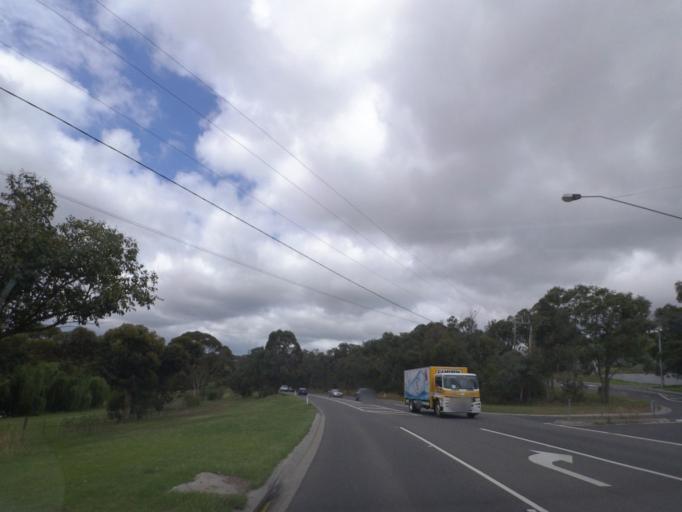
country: AU
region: Victoria
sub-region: Nillumbik
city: Diamond Creek
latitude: -37.6762
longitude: 145.1338
